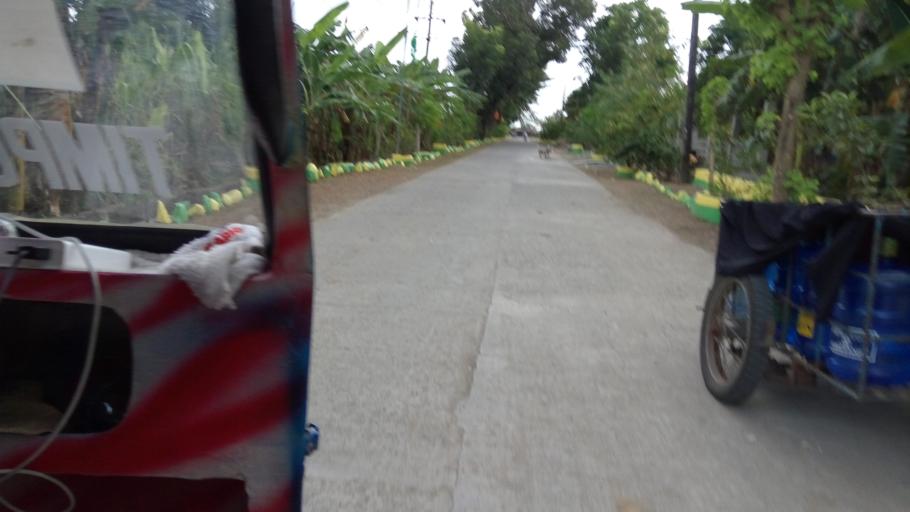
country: PH
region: Ilocos
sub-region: Province of La Union
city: Santo Tomas
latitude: 16.2854
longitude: 120.3826
